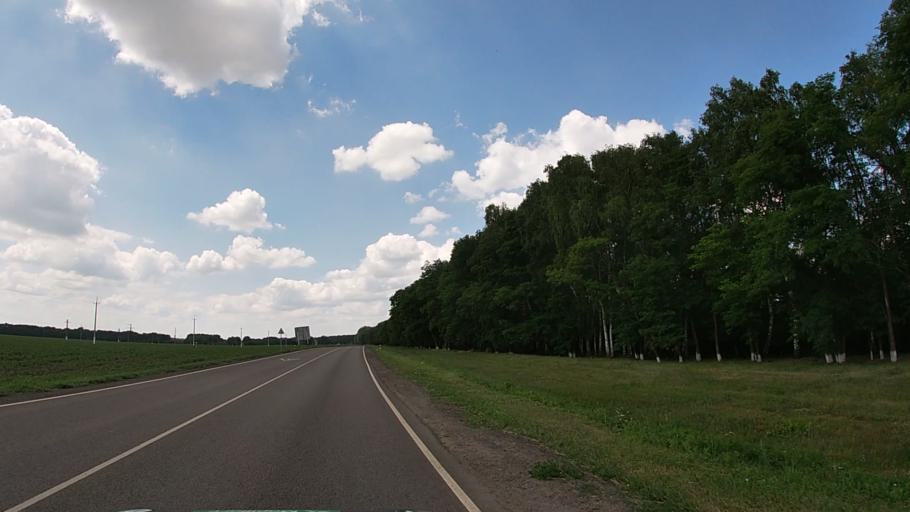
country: RU
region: Belgorod
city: Grayvoron
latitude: 50.5037
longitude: 35.7376
